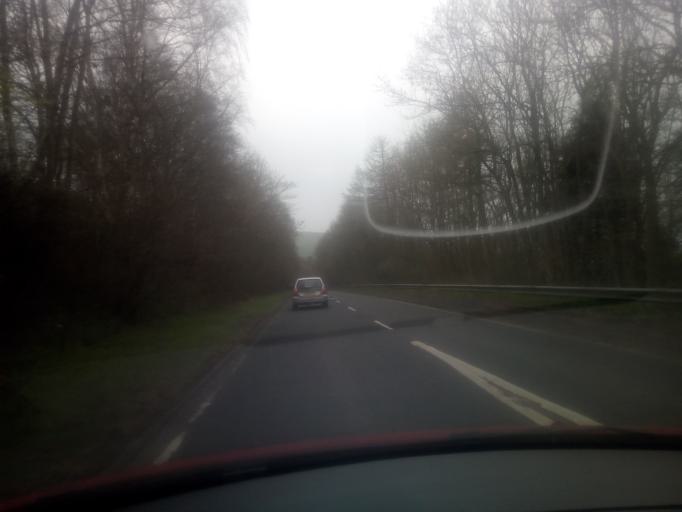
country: GB
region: Scotland
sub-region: The Scottish Borders
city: Galashiels
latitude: 55.6354
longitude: -2.8271
